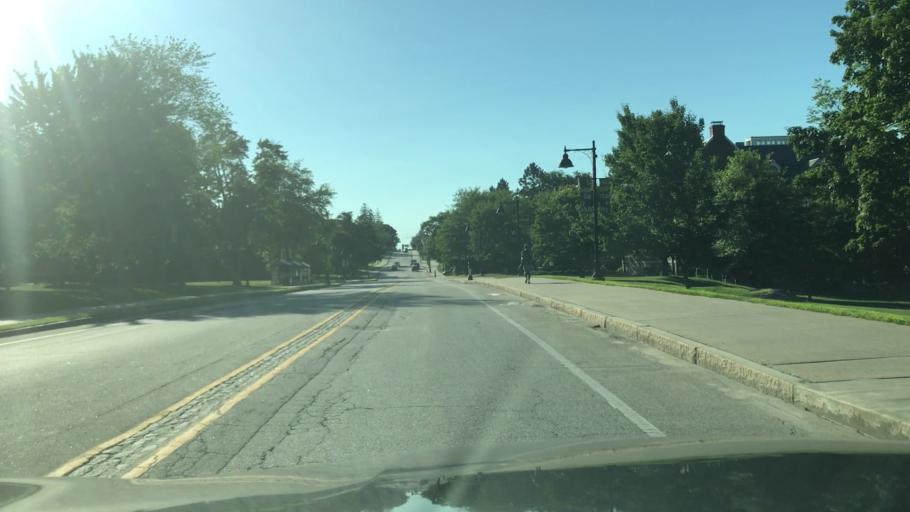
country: US
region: New Hampshire
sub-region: Strafford County
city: Durham
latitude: 43.1367
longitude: -70.9315
